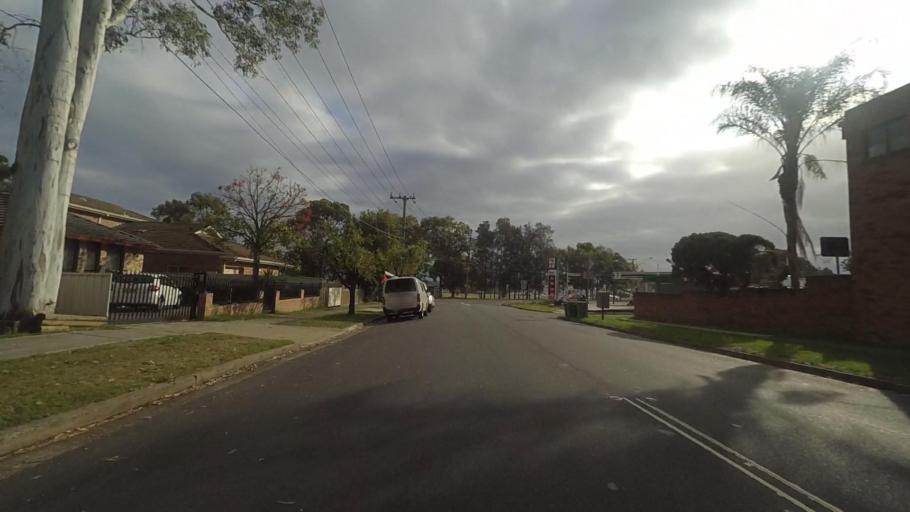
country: AU
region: New South Wales
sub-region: Bankstown
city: Milperra
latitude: -33.9152
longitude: 150.9983
